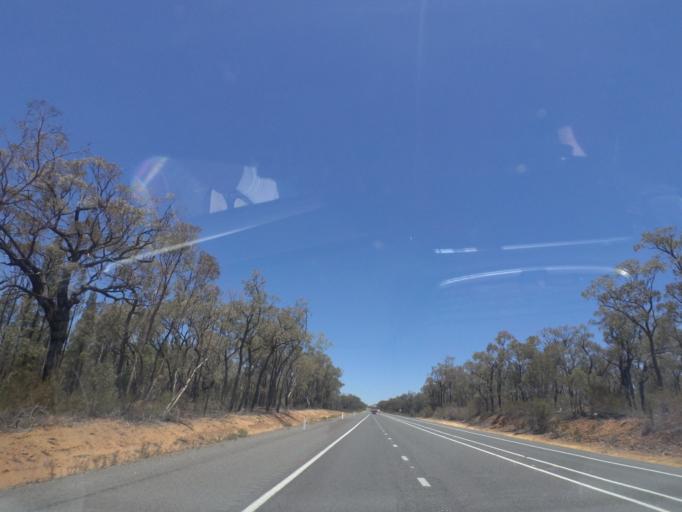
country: AU
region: New South Wales
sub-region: Warrumbungle Shire
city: Coonabarabran
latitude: -30.9050
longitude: 149.4380
